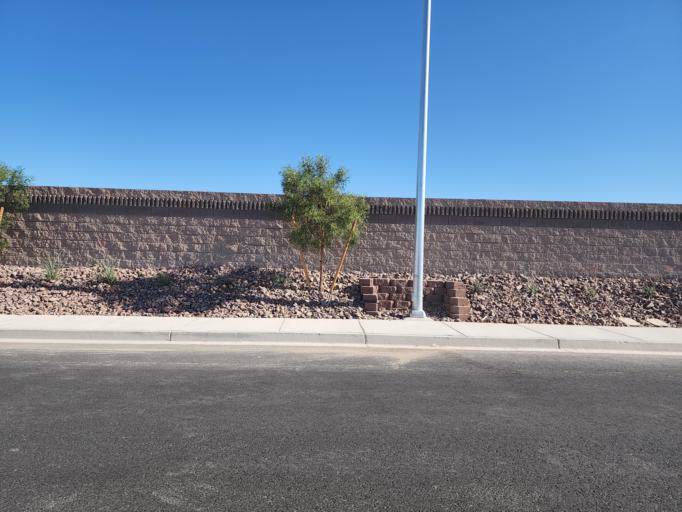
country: US
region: Nevada
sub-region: Clark County
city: Spring Valley
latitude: 36.0813
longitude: -115.2673
